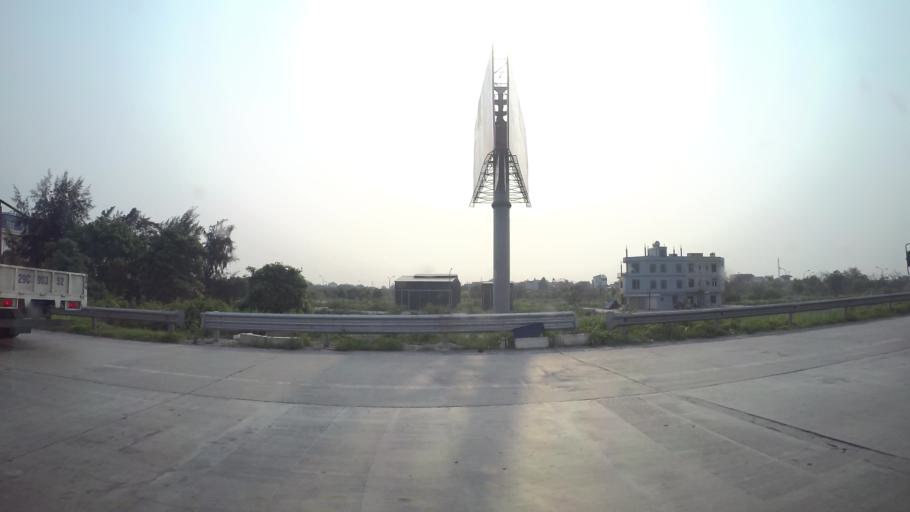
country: VN
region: Ha Noi
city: Thuong Tin
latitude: 20.9085
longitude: 105.8609
